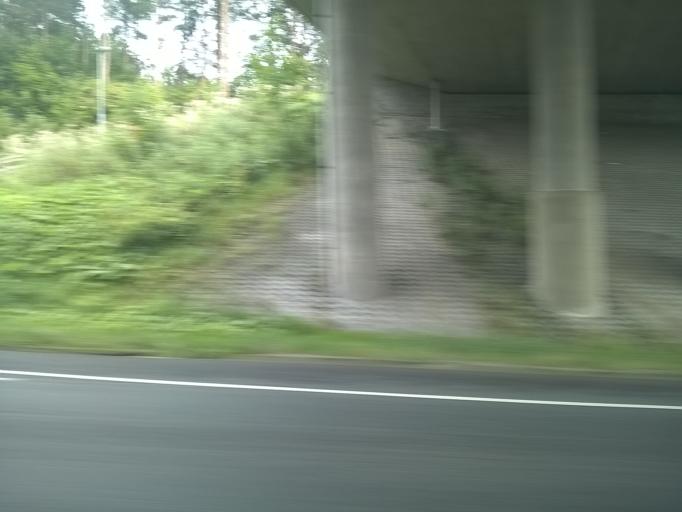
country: FI
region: Pirkanmaa
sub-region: Tampere
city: Tampere
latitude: 61.4871
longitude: 23.8260
